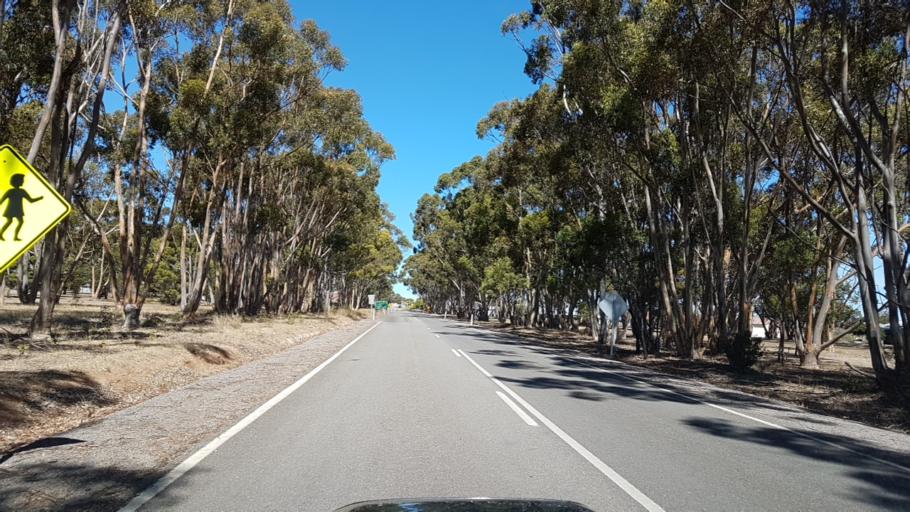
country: AU
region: South Australia
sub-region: Yorke Peninsula
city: Maitland
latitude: -34.3691
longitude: 137.6711
